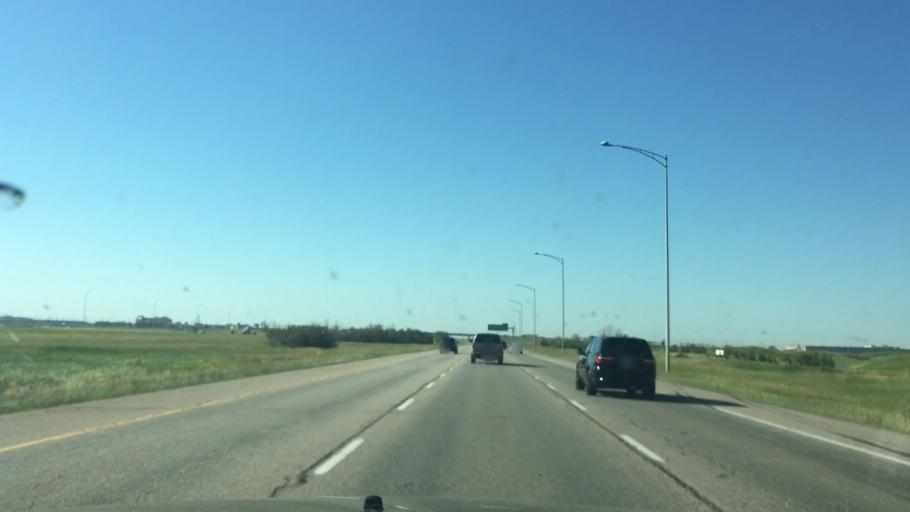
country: CA
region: Alberta
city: Leduc
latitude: 53.3201
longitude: -113.5498
